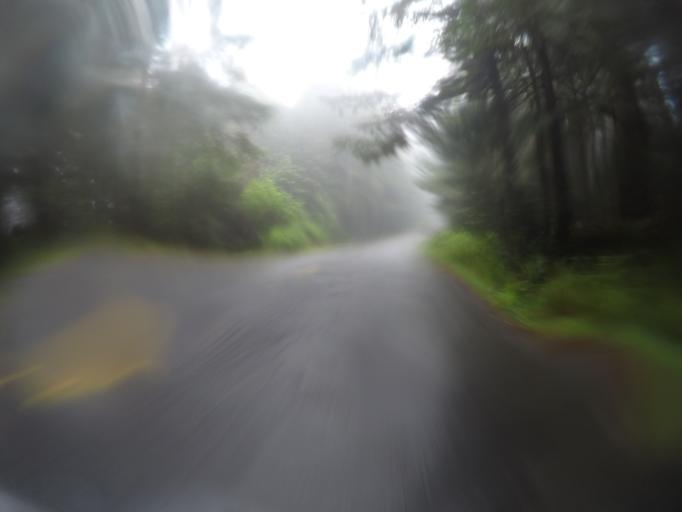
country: US
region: California
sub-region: Humboldt County
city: Westhaven-Moonstone
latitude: 41.2703
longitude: -123.9972
